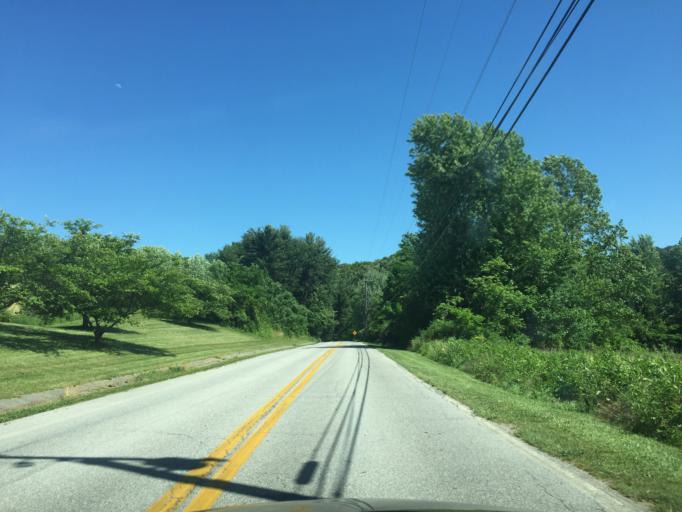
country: US
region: Maryland
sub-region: Carroll County
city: Manchester
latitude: 39.6175
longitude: -76.8929
